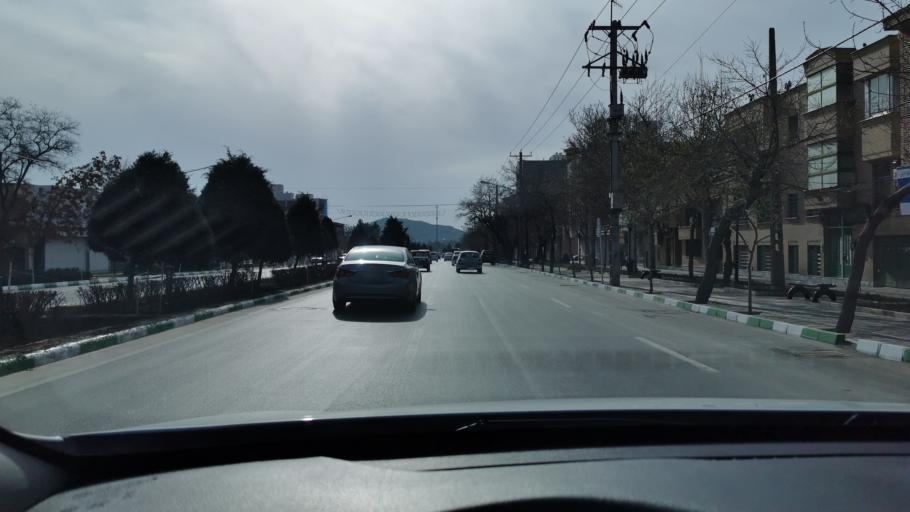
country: IR
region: Razavi Khorasan
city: Mashhad
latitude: 36.2861
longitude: 59.5459
